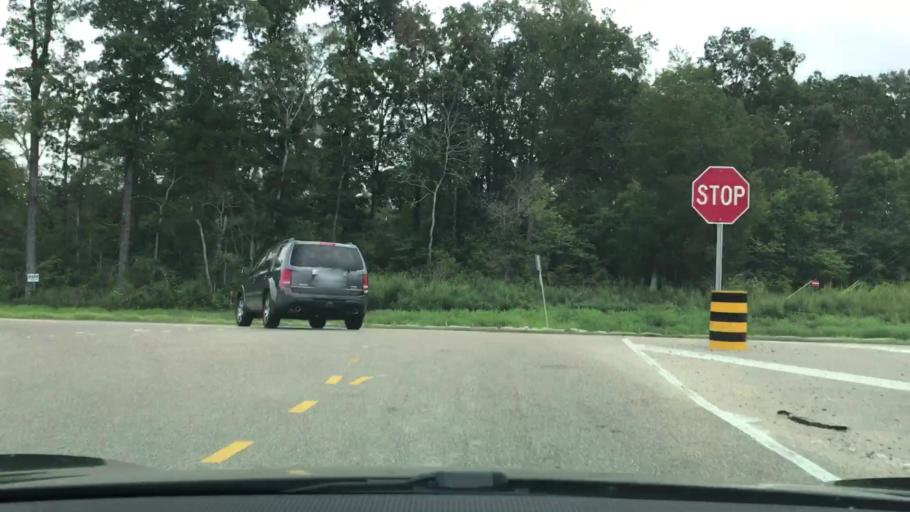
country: US
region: Alabama
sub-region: Montgomery County
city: Pike Road
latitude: 32.3142
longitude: -86.0470
